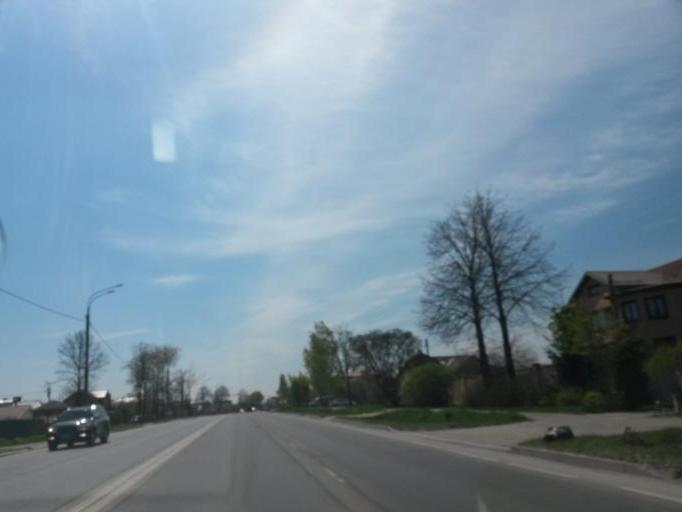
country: RU
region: Moskovskaya
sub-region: Podol'skiy Rayon
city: Podol'sk
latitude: 55.3975
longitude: 37.5493
